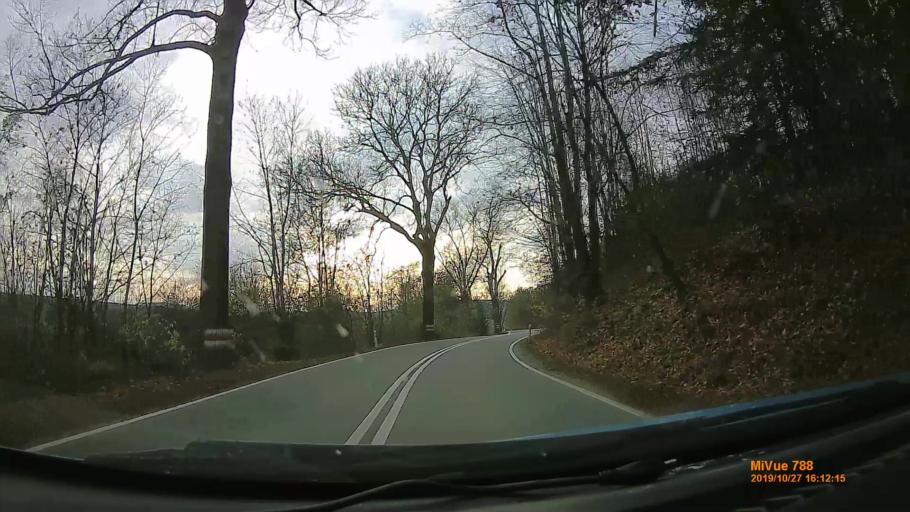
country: PL
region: Lower Silesian Voivodeship
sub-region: Powiat klodzki
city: Radkow
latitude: 50.5533
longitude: 16.4184
